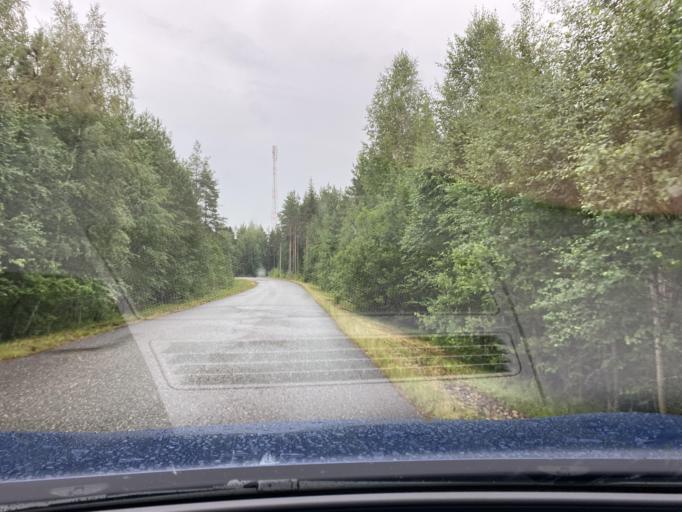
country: FI
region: Central Ostrobothnia
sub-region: Kaustinen
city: Halsua
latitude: 63.4172
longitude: 23.9761
